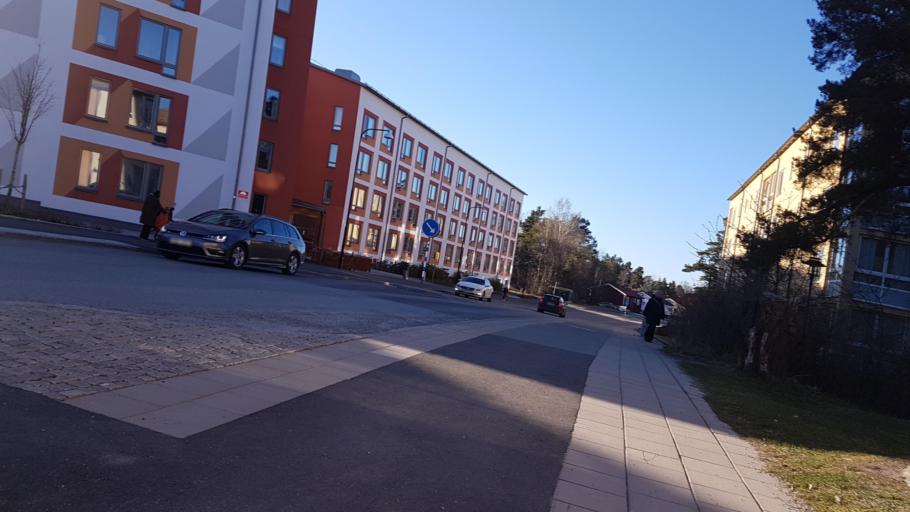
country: SE
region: Stockholm
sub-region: Stockholms Kommun
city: Arsta
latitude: 59.2641
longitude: 18.0831
